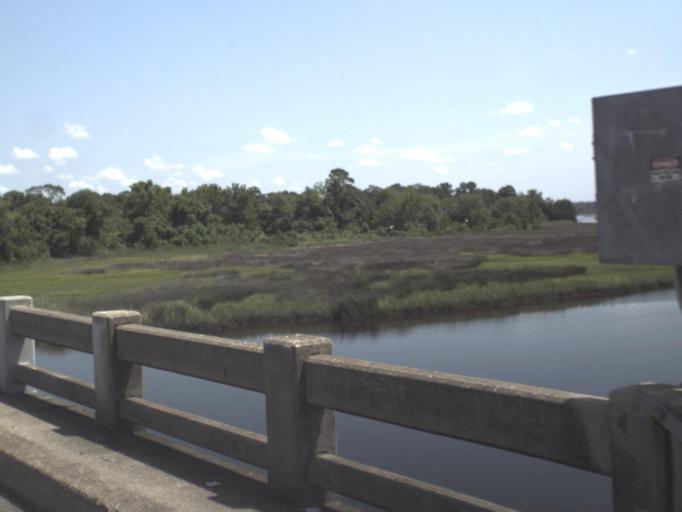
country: US
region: Florida
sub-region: Duval County
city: Jacksonville
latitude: 30.3951
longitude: -81.6825
